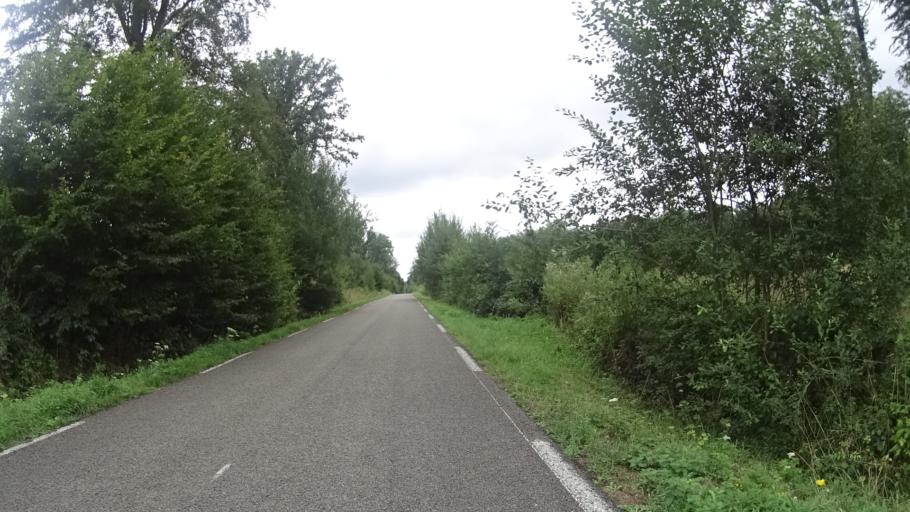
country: FR
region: Nord-Pas-de-Calais
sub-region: Departement du Nord
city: Maroilles
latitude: 50.1634
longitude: 3.7669
